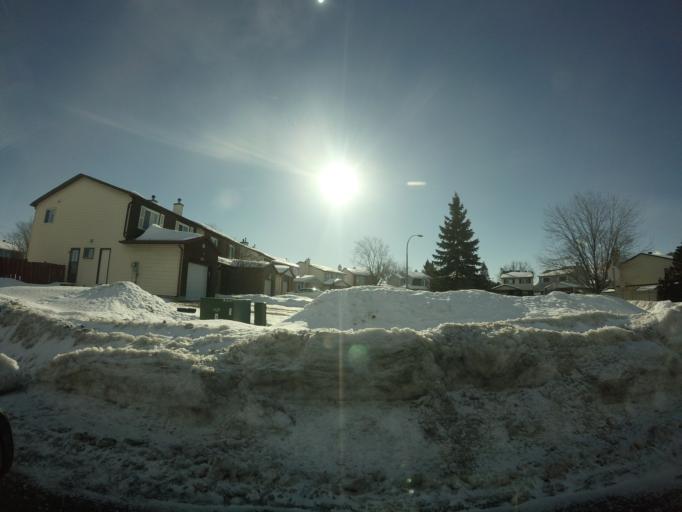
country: CA
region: Ontario
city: Ottawa
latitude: 45.4239
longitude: -75.6121
